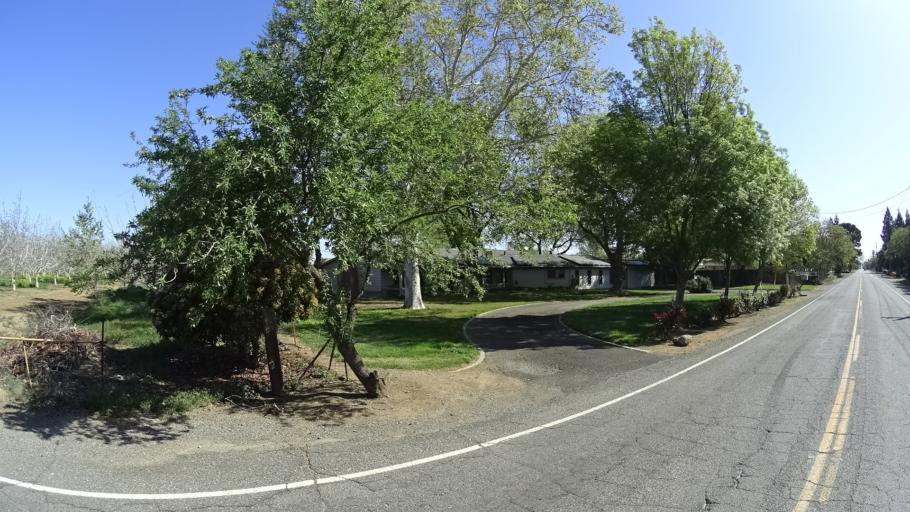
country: US
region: California
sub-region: Glenn County
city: Willows
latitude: 39.5388
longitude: -122.2027
